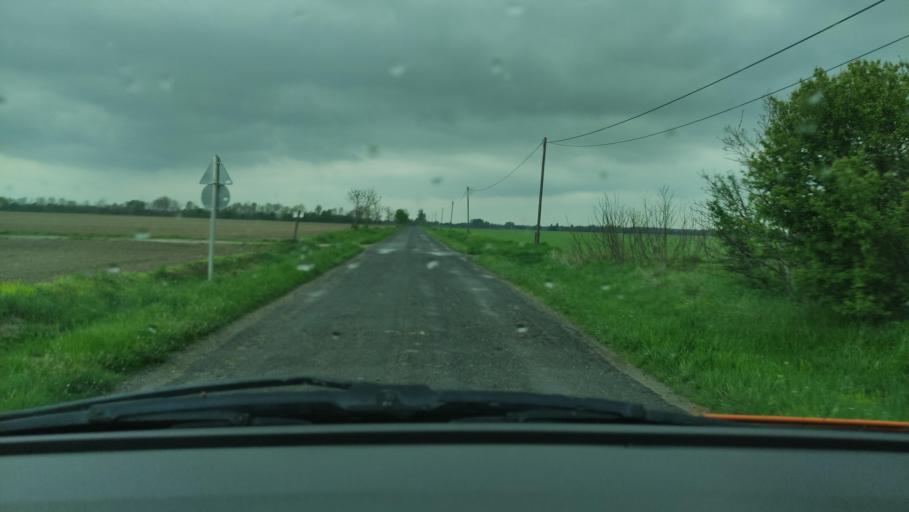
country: HU
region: Baranya
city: Mohacs
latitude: 45.9300
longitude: 18.7054
